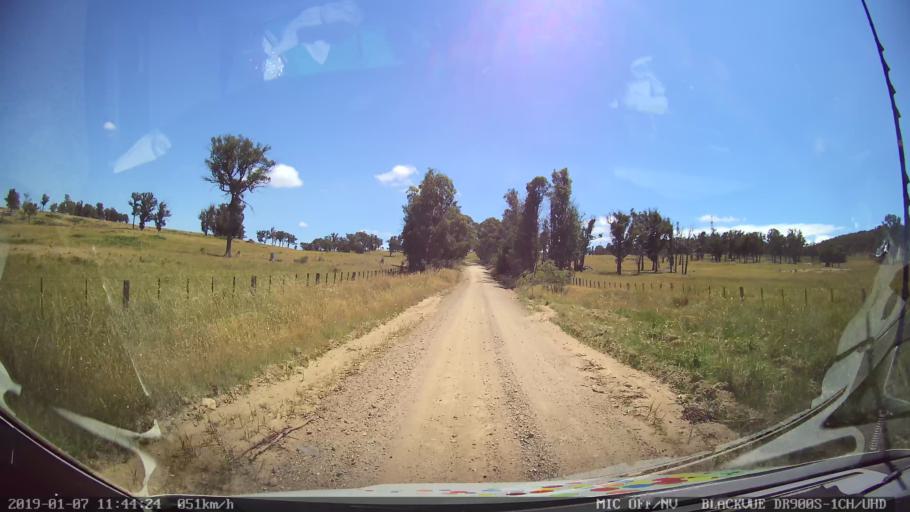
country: AU
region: New South Wales
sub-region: Guyra
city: Guyra
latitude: -30.3529
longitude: 151.6063
